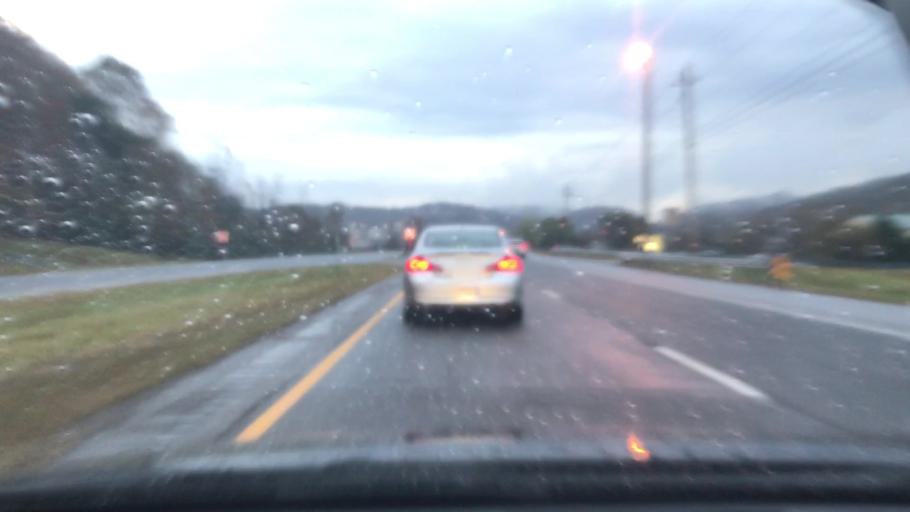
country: US
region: Tennessee
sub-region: Cheatham County
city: Ashland City
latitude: 36.2493
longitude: -87.0317
